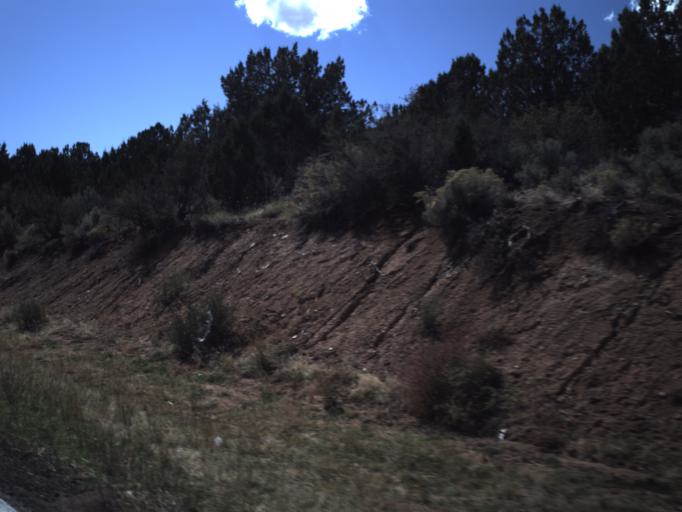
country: US
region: Utah
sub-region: Washington County
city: Enterprise
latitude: 37.5572
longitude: -113.6904
